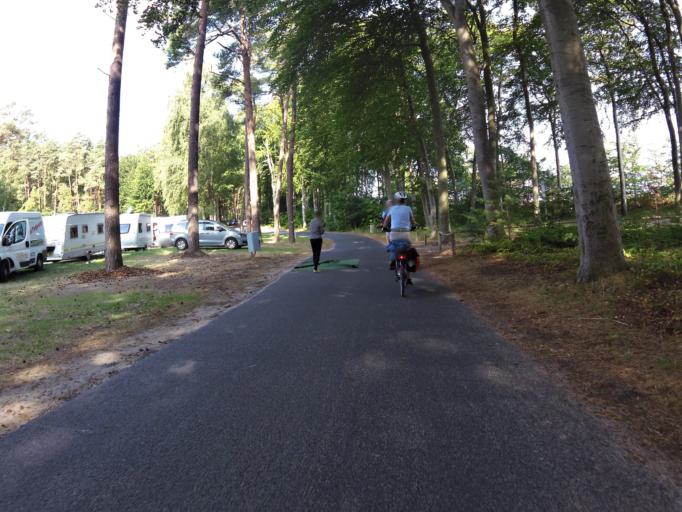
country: DE
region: Mecklenburg-Vorpommern
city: Seebad Bansin
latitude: 54.0013
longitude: 14.0973
